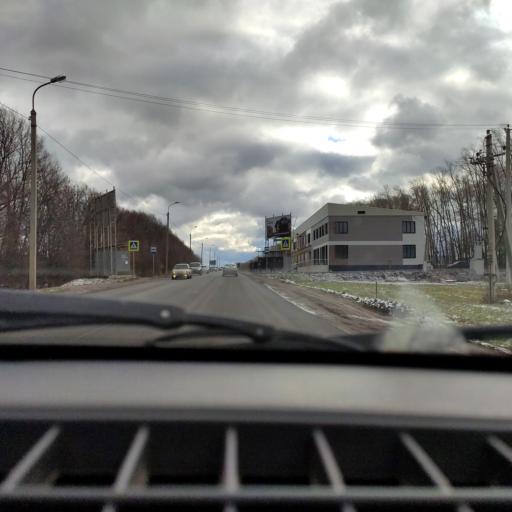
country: RU
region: Bashkortostan
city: Kabakovo
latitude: 54.6319
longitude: 56.0973
